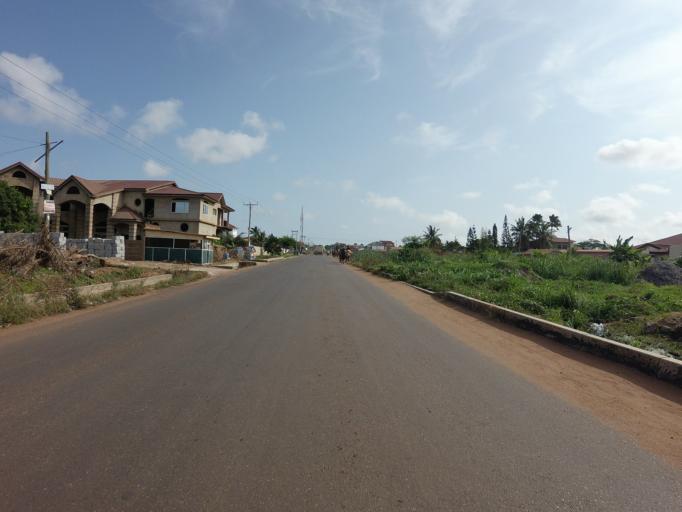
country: GH
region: Greater Accra
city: Nungua
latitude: 5.6445
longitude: -0.1005
